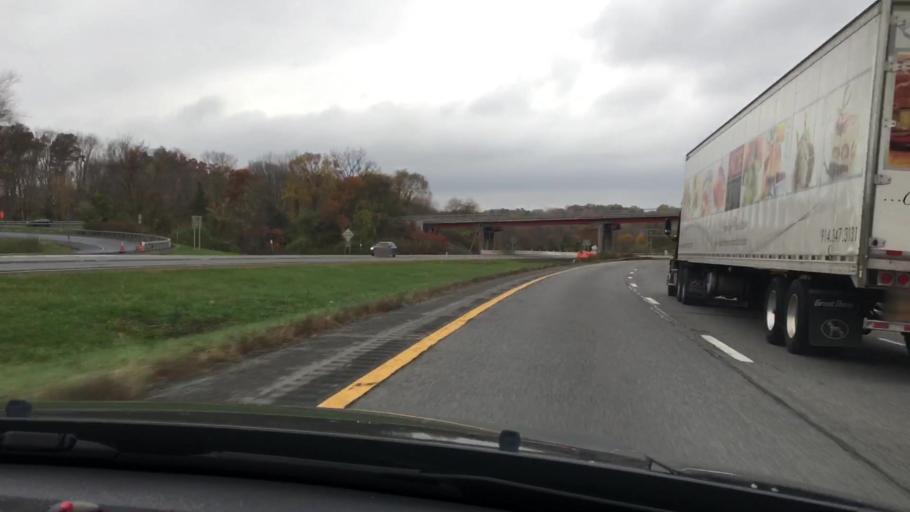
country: US
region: New York
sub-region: Putnam County
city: Brewster
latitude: 41.3912
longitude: -73.5986
